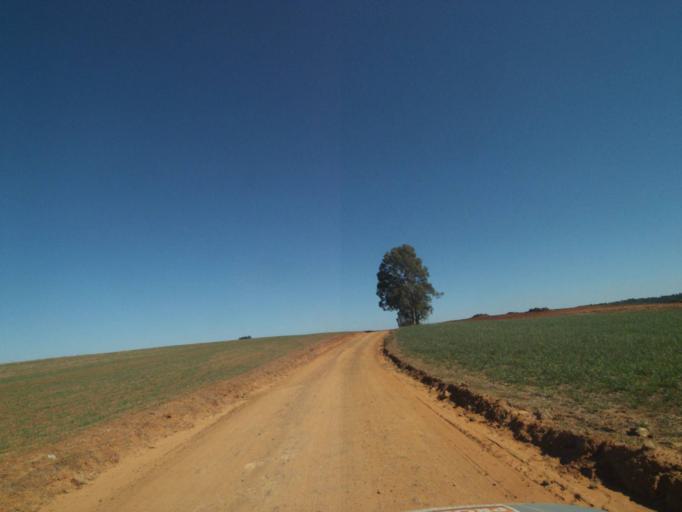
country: BR
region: Parana
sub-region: Tibagi
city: Tibagi
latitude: -24.5617
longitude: -50.6231
